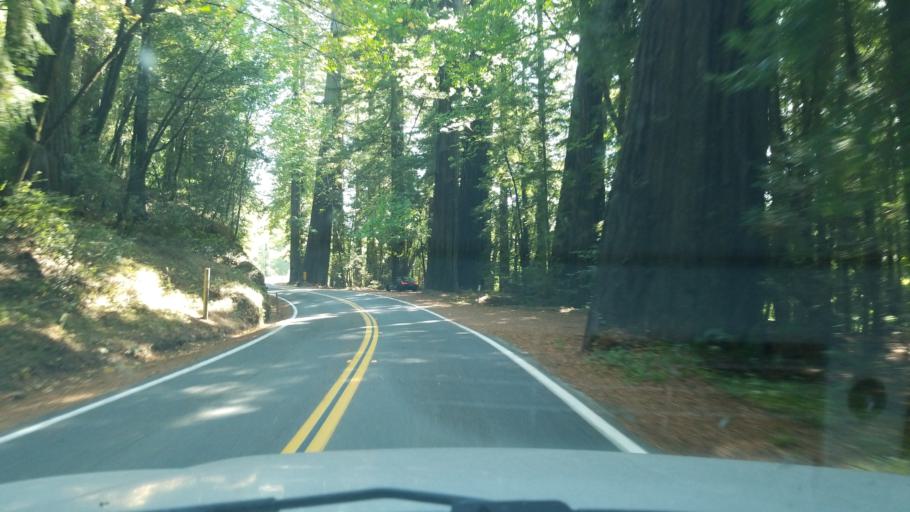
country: US
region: California
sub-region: Humboldt County
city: Redway
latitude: 40.2510
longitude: -123.8227
